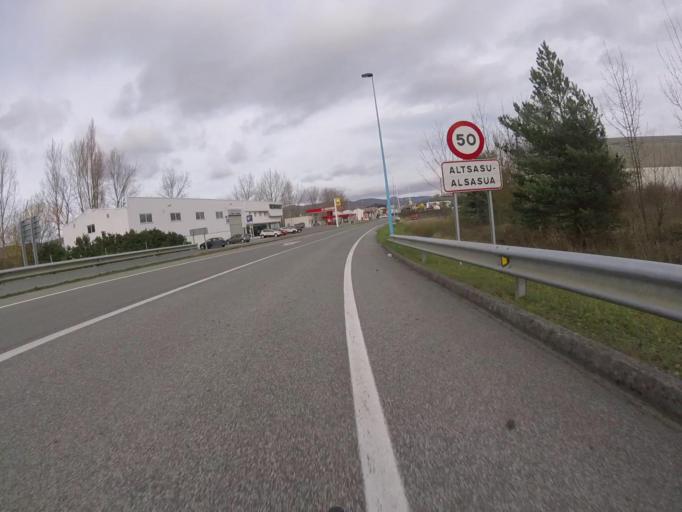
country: ES
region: Navarre
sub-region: Provincia de Navarra
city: Altsasu
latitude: 42.8891
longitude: -2.1698
